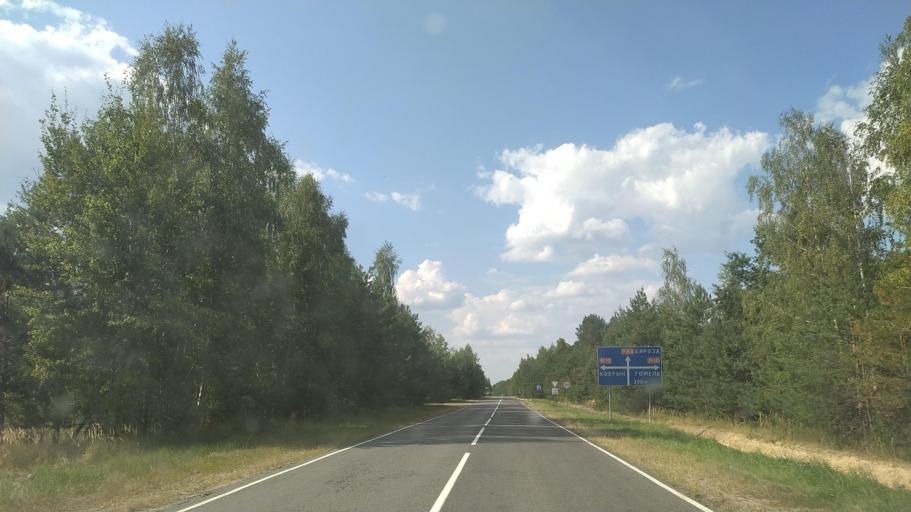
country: BY
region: Brest
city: Drahichyn
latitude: 52.2193
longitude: 25.1269
